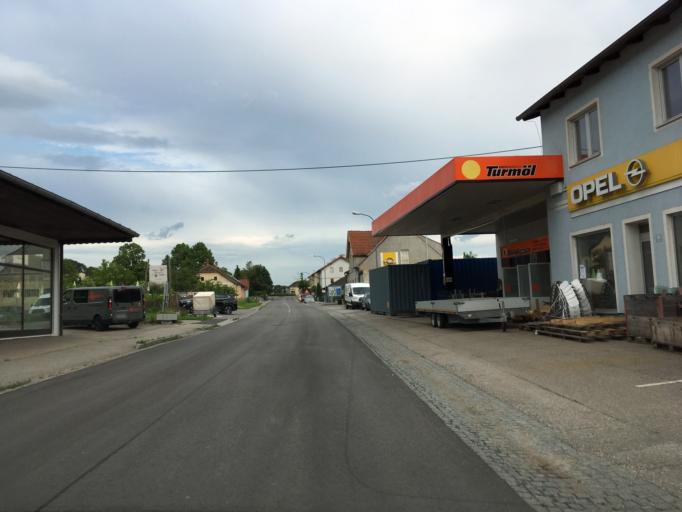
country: AT
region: Lower Austria
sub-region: Politischer Bezirk Tulln
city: Kirchberg am Wagram
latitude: 48.4321
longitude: 15.8977
